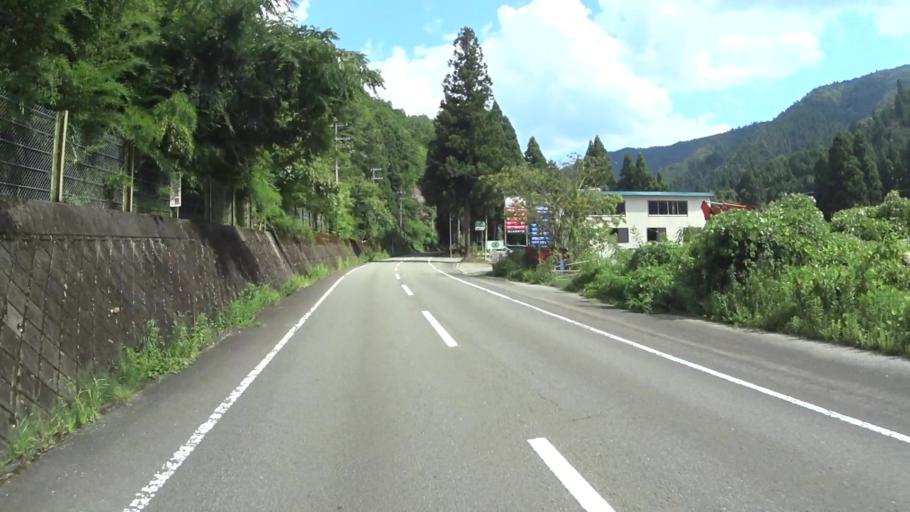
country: JP
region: Fukui
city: Obama
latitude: 35.2734
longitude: 135.5915
